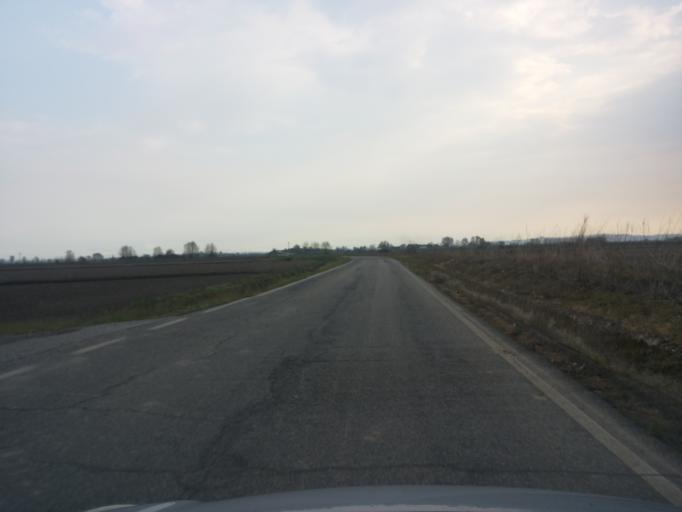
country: IT
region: Piedmont
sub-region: Provincia di Vercelli
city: Caresana
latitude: 45.2019
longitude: 8.4972
